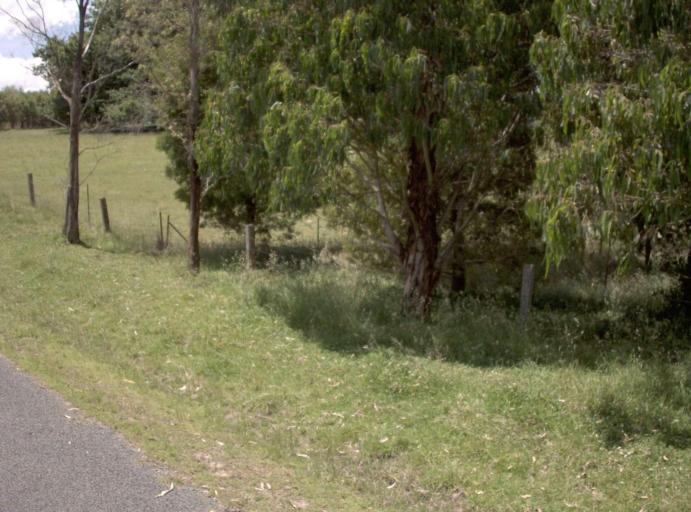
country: AU
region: New South Wales
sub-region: Bombala
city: Bombala
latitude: -37.4113
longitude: 149.0095
